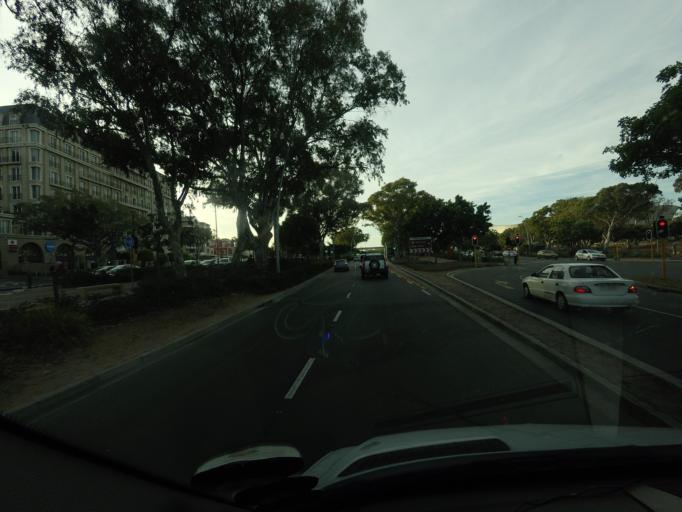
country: ZA
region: Western Cape
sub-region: City of Cape Town
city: Cape Town
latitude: -33.9088
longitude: 18.4131
